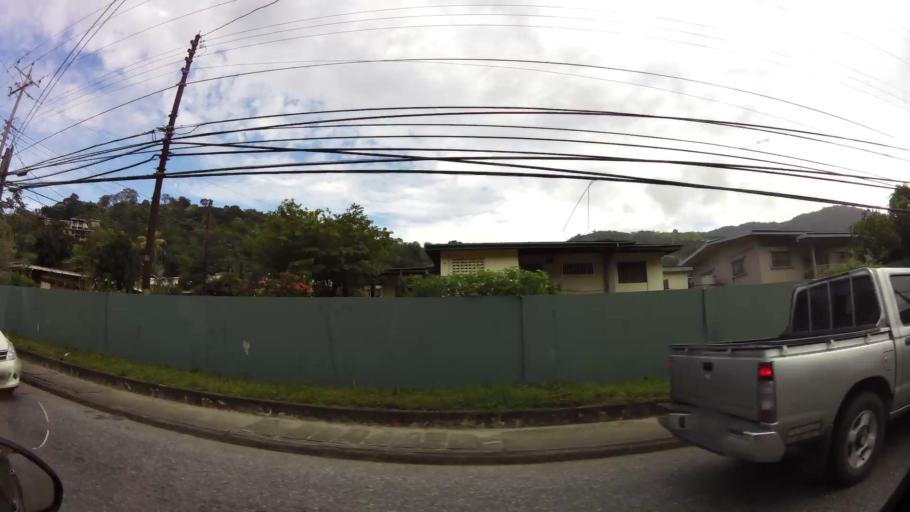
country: TT
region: San Juan/Laventille
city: Laventille
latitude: 10.6783
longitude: -61.4541
